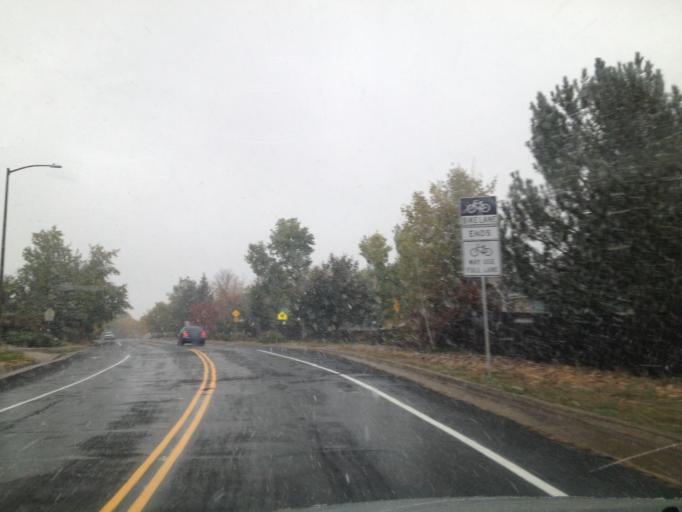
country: US
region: Colorado
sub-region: Boulder County
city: Louisville
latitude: 39.9825
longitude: -105.1543
